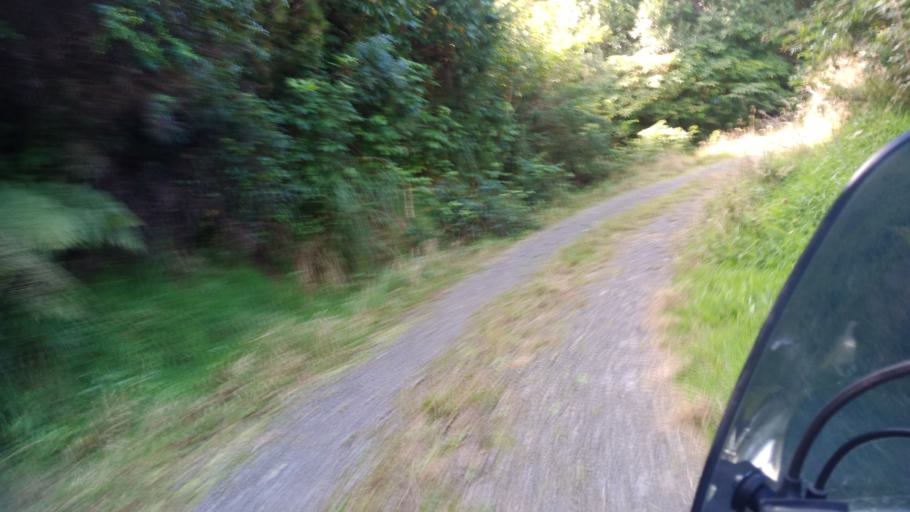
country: NZ
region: Hawke's Bay
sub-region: Wairoa District
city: Wairoa
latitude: -39.0037
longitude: 177.0841
